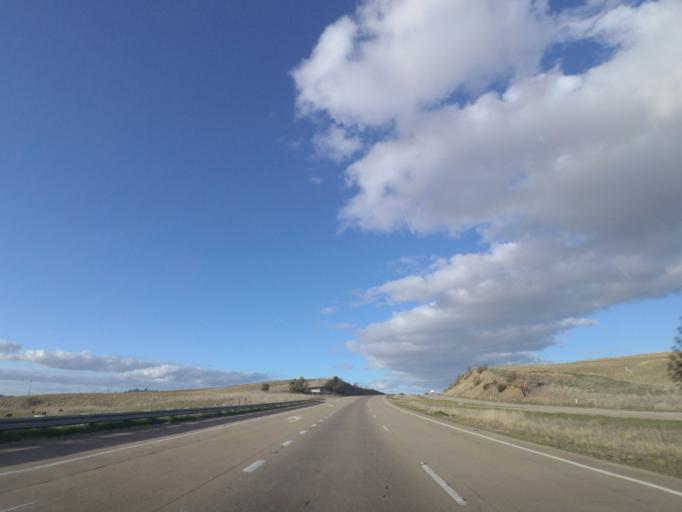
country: AU
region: New South Wales
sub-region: Gundagai
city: Gundagai
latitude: -34.8120
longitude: 148.4502
